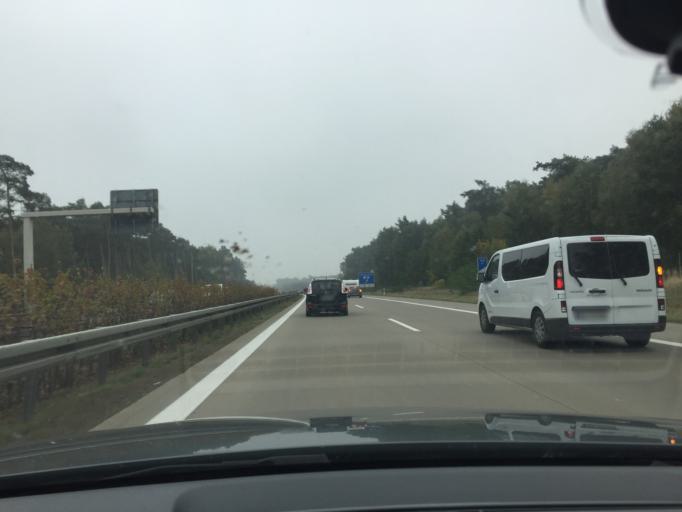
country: DE
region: Brandenburg
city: Luebben
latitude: 51.8913
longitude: 13.8301
